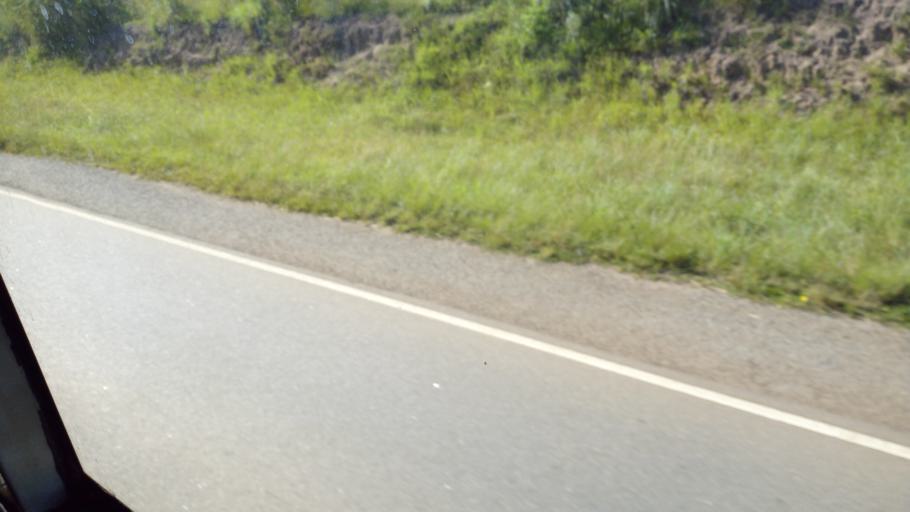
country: UG
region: Central Region
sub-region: Lyantonde District
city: Lyantonde
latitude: -0.4547
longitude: 31.0520
